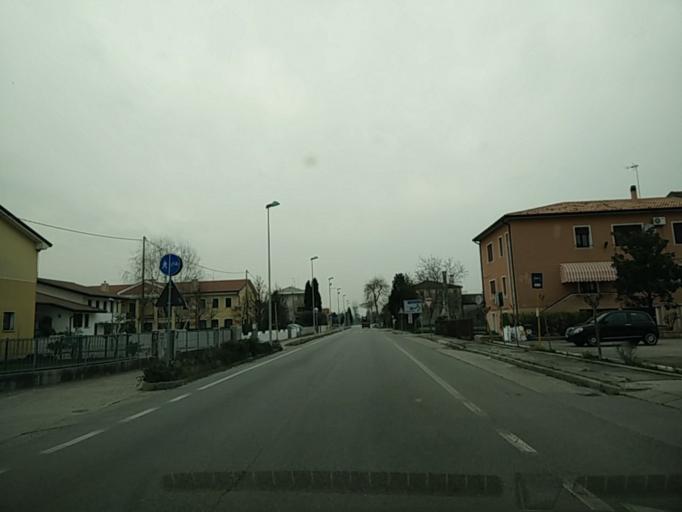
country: IT
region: Veneto
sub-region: Provincia di Padova
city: Massanzago-Ca' Baglioni-San Dono
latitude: 45.5544
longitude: 12.0287
